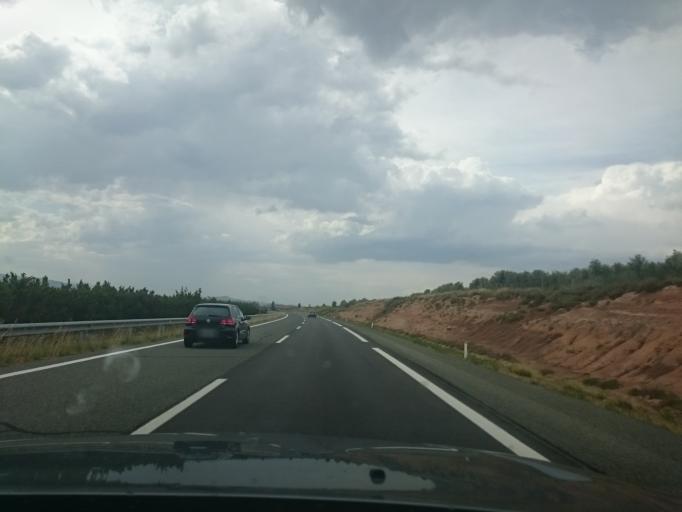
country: ES
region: Navarre
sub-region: Provincia de Navarra
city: Corella
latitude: 42.1460
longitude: -1.7864
